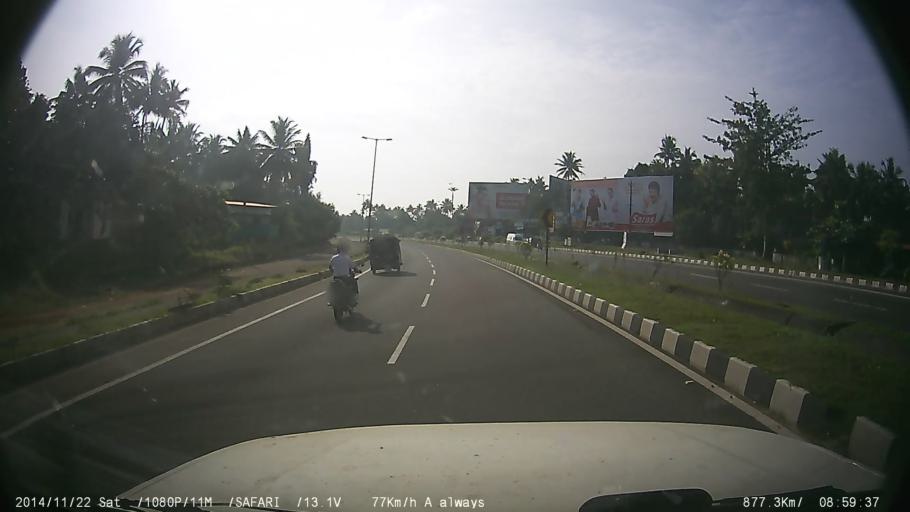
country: IN
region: Kerala
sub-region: Thrissur District
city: Irinjalakuda
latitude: 10.3877
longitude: 76.2887
